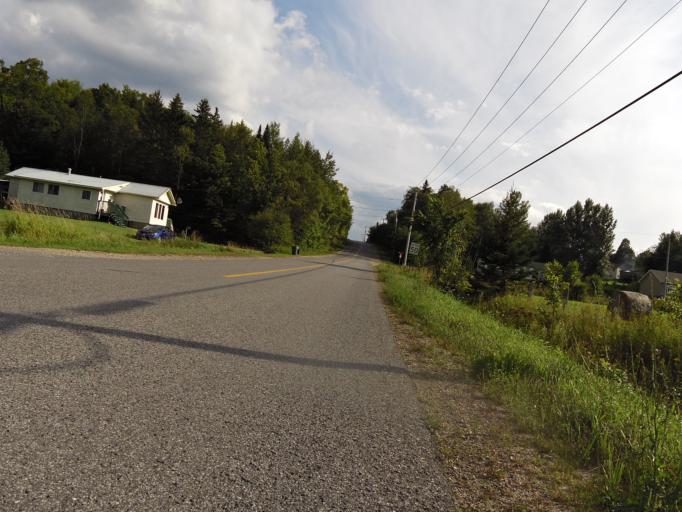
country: CA
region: Quebec
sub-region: Outaouais
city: Wakefield
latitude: 45.6530
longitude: -76.0163
